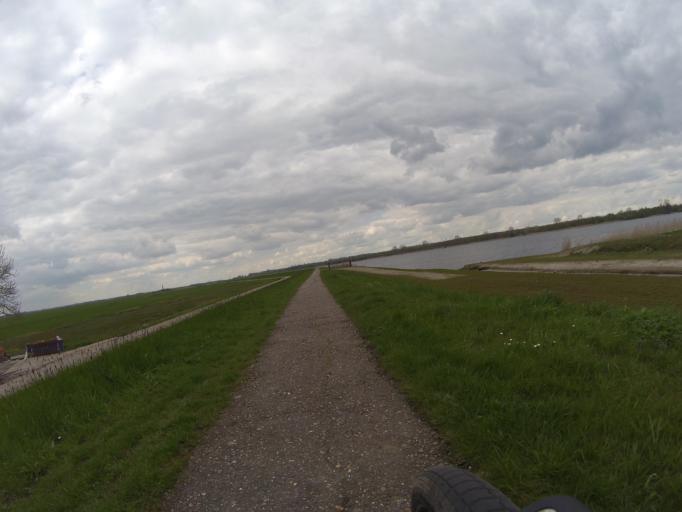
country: NL
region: Gelderland
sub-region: Gemeente Nijkerk
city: Nijkerk
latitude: 52.2533
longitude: 5.4551
